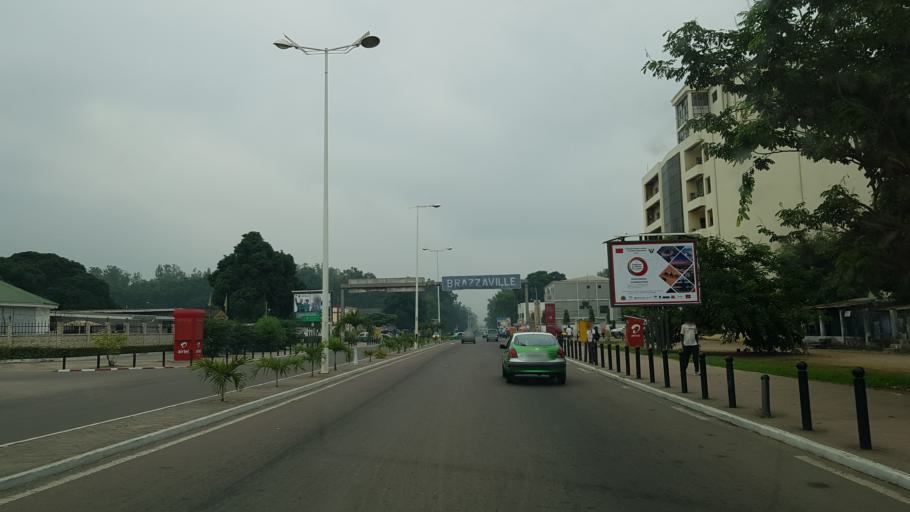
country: CG
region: Brazzaville
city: Brazzaville
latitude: -4.2632
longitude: 15.2526
